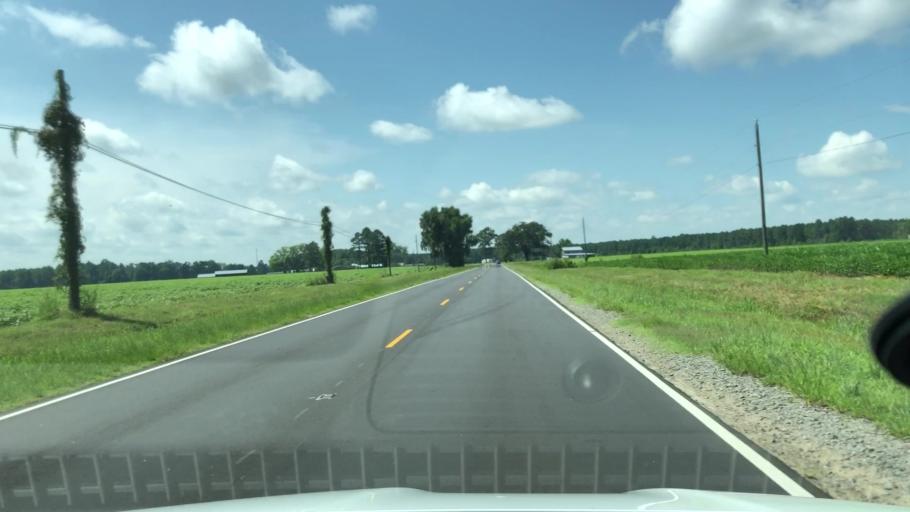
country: US
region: North Carolina
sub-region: Martin County
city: Williamston
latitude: 35.7680
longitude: -77.0714
